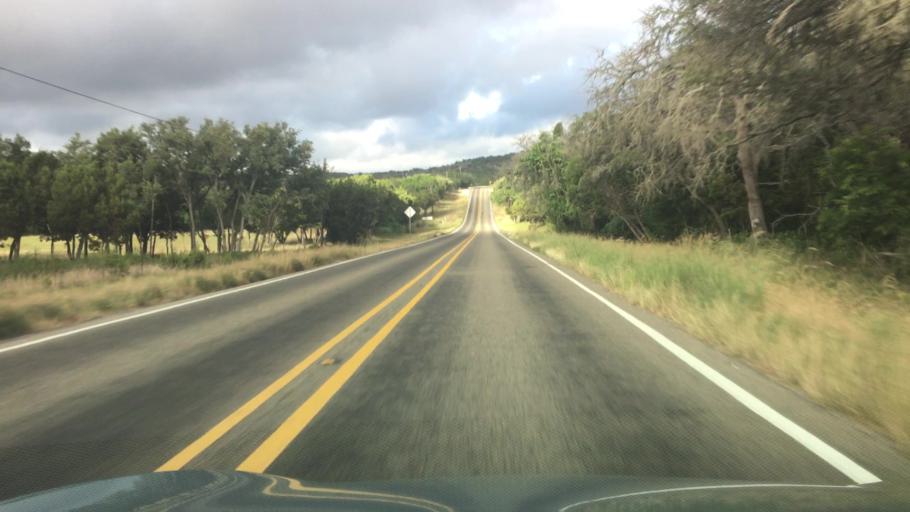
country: US
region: Texas
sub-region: Hays County
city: Dripping Springs
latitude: 30.1585
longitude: -98.2472
